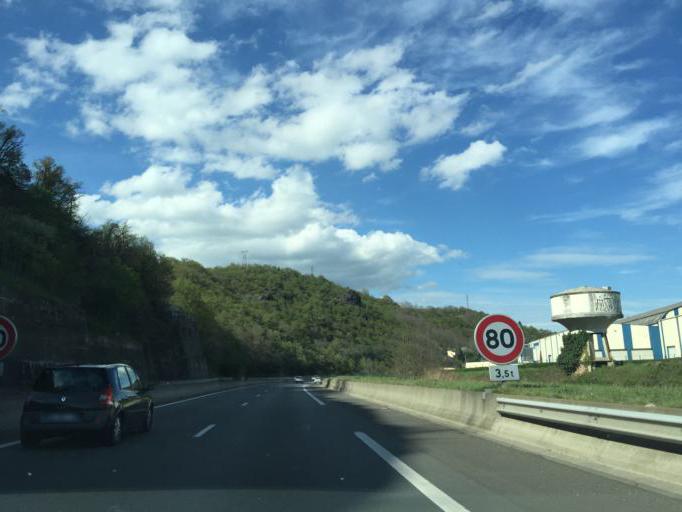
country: FR
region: Rhone-Alpes
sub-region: Departement de la Loire
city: Lorette
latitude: 45.5103
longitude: 4.5690
